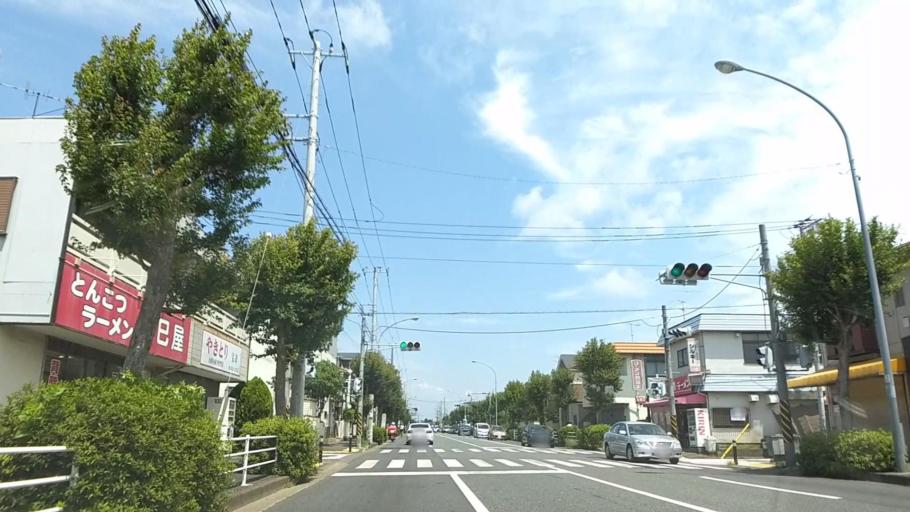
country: JP
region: Kanagawa
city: Minami-rinkan
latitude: 35.4439
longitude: 139.4844
